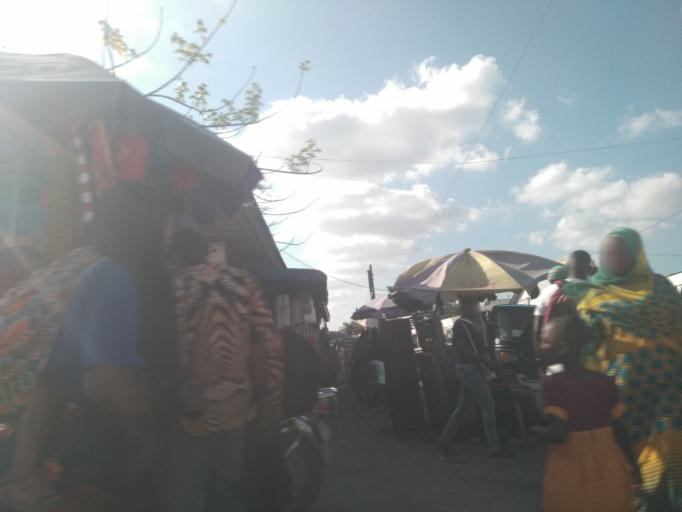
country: TZ
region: Dar es Salaam
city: Dar es Salaam
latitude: -6.8672
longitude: 39.2616
